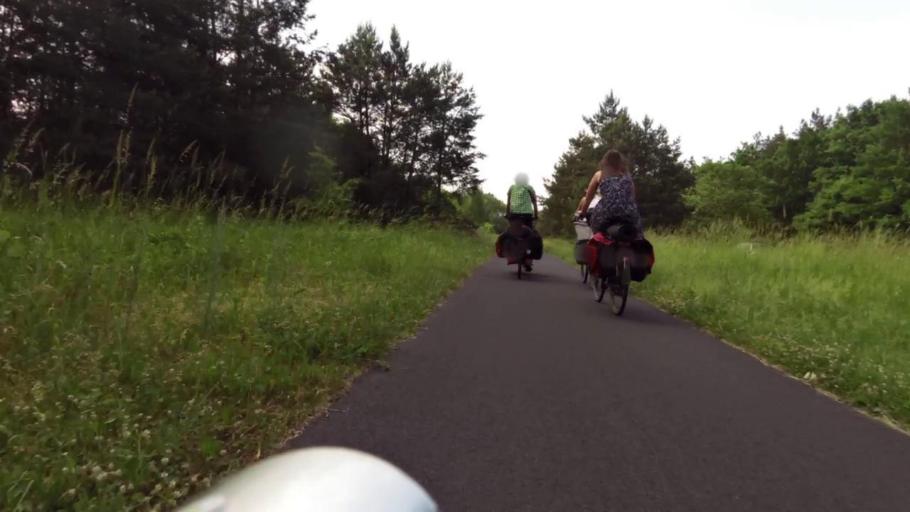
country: PL
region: Kujawsko-Pomorskie
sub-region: Powiat torunski
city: Lysomice
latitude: 53.0770
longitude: 18.5419
